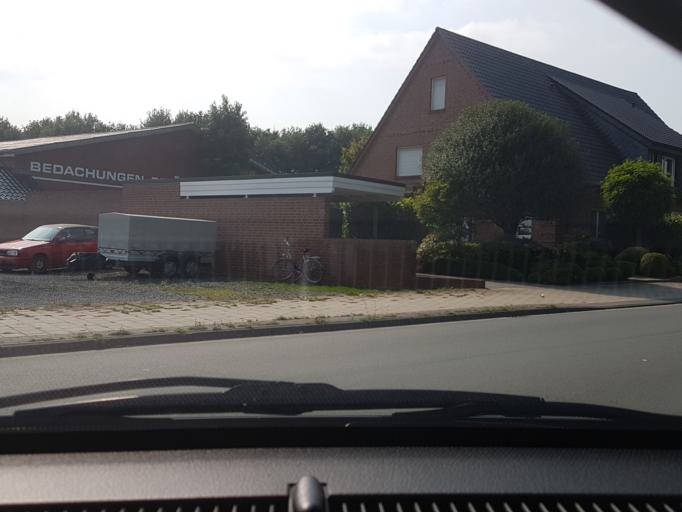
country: DE
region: North Rhine-Westphalia
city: Emsdetten
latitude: 52.1607
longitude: 7.5595
